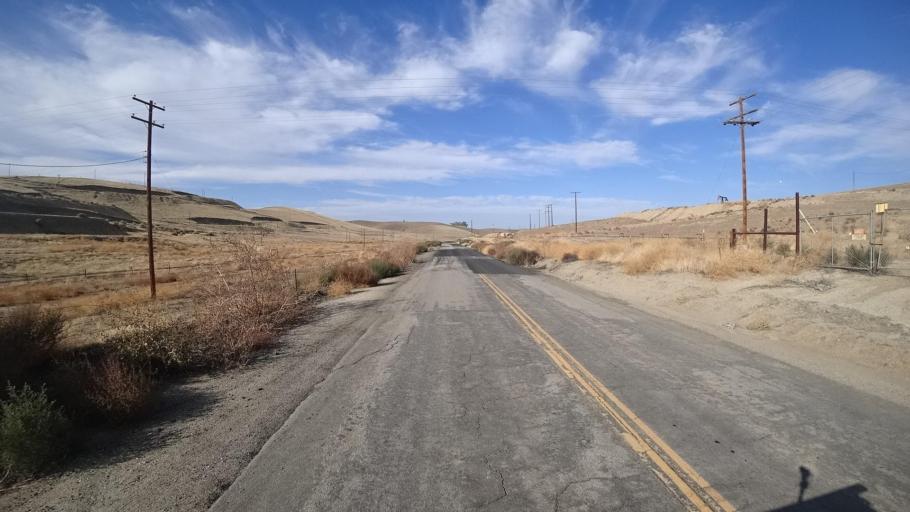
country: US
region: California
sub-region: Kern County
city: Oildale
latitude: 35.6121
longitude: -118.9754
